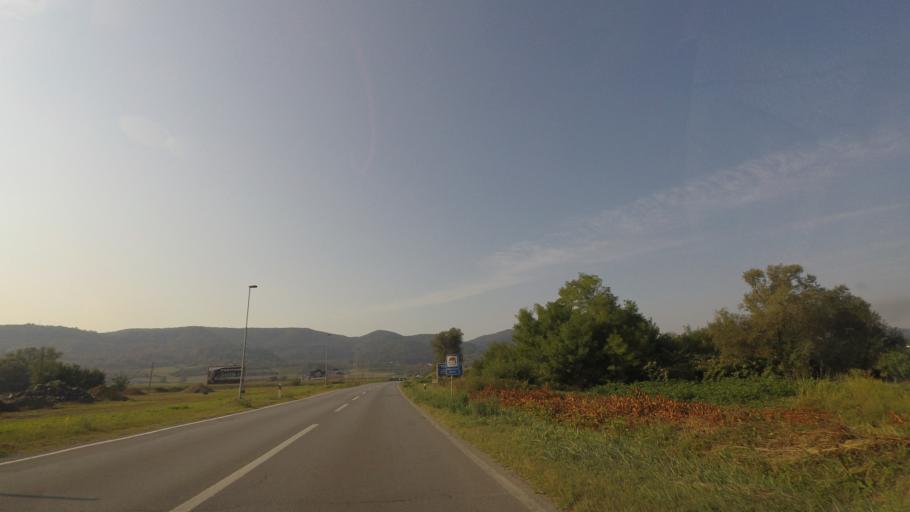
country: HR
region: Pozesko-Slavonska
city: Pozega
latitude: 45.3356
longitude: 17.6522
